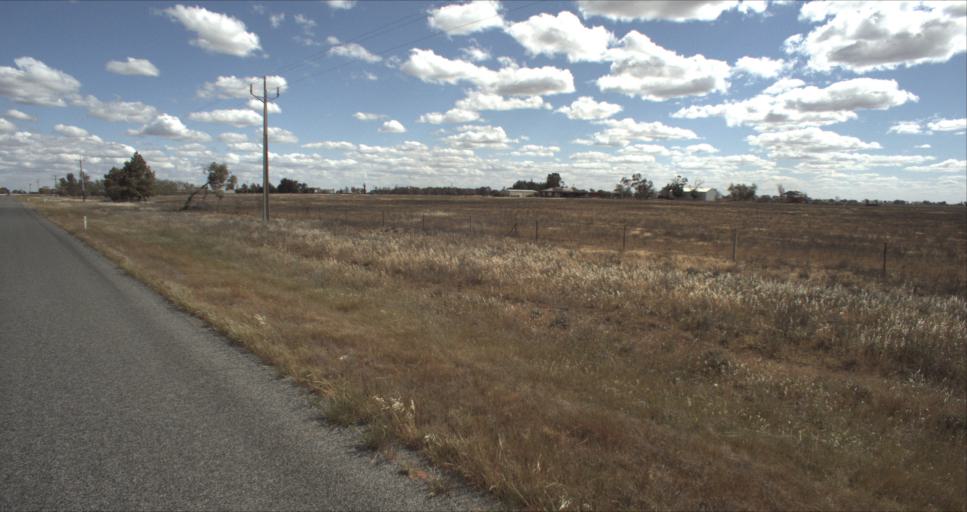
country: AU
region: New South Wales
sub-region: Leeton
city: Leeton
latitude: -34.4557
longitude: 146.2537
